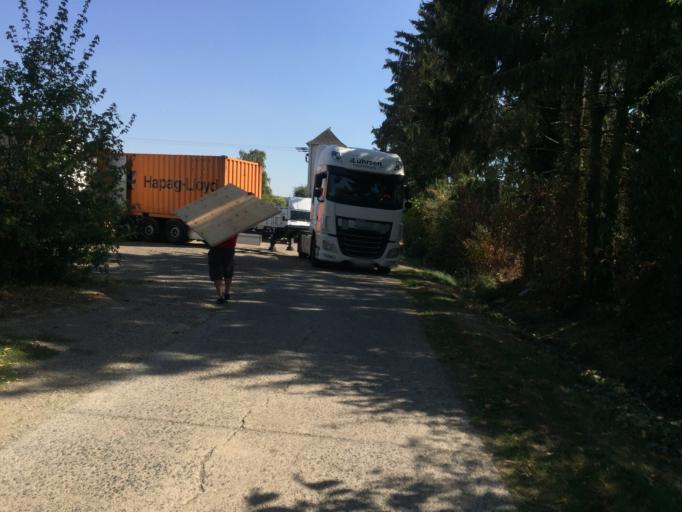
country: DE
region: Hesse
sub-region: Regierungsbezirk Giessen
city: Hungen
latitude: 50.4375
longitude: 8.8878
